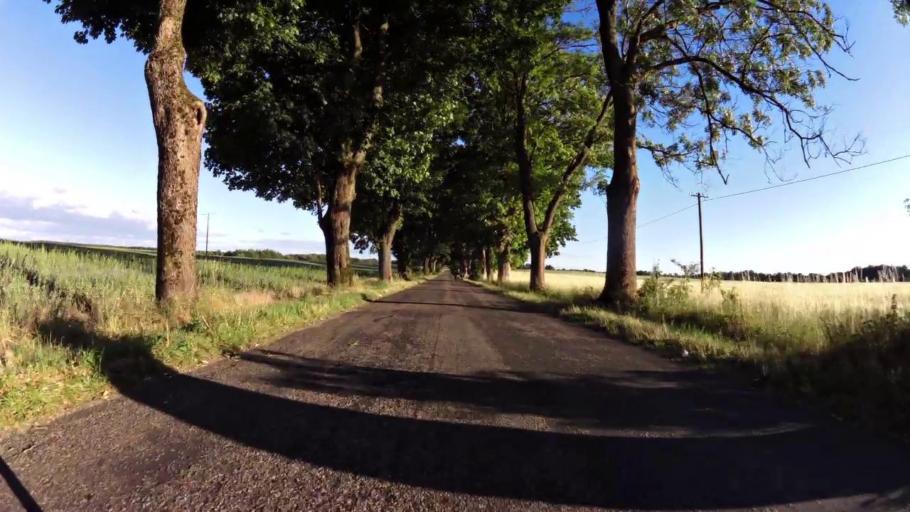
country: PL
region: West Pomeranian Voivodeship
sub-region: Powiat swidwinski
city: Swidwin
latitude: 53.7515
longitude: 15.6900
